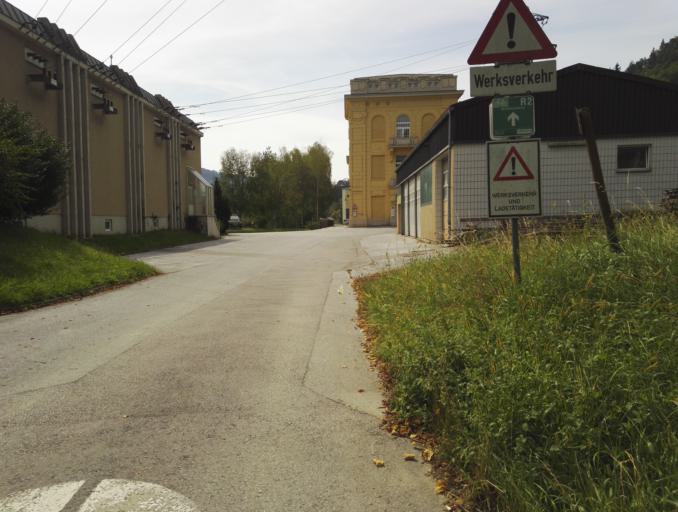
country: AT
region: Styria
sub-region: Politischer Bezirk Graz-Umgebung
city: Peggau
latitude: 47.2101
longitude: 15.3359
